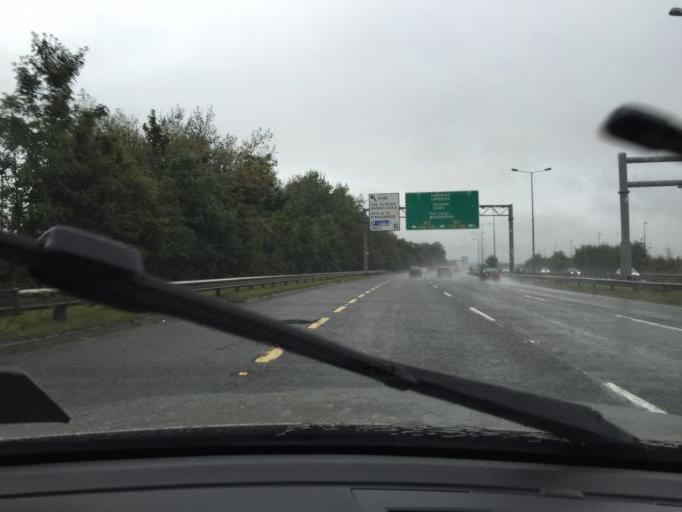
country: IE
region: Leinster
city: Clondalkin
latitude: 53.3071
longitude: -6.4059
